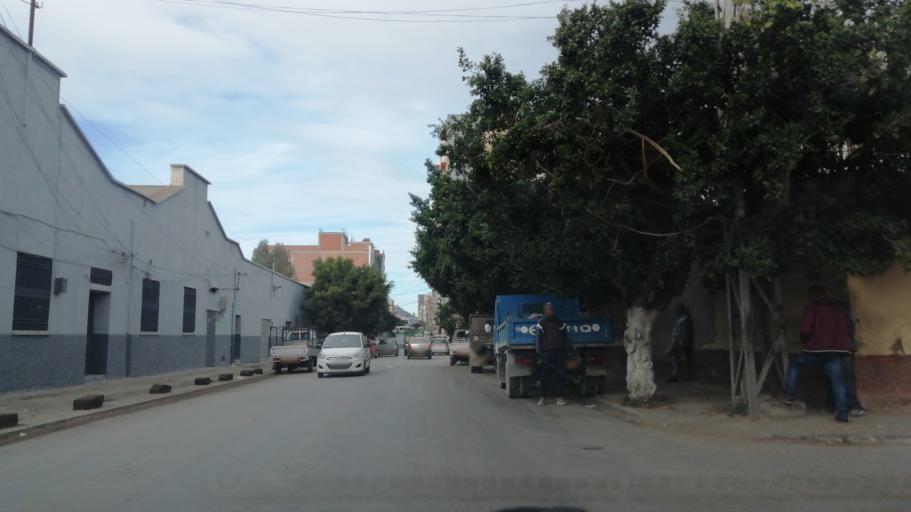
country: DZ
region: Oran
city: Oran
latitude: 35.6875
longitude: -0.6206
